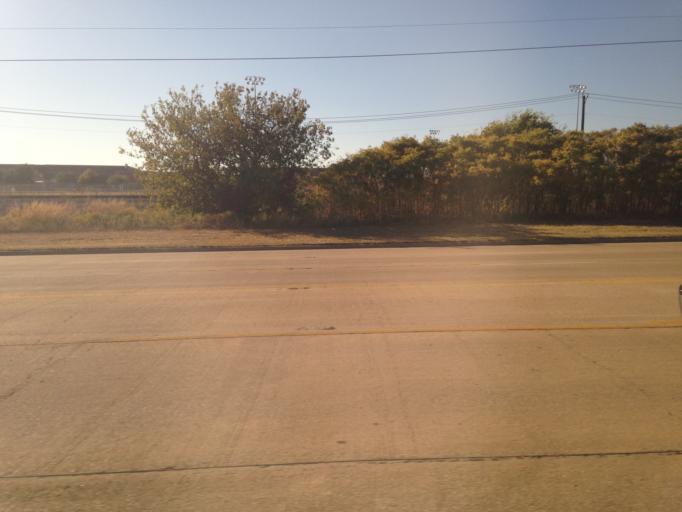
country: US
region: Texas
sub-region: Tarrant County
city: Watauga
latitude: 32.8894
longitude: -97.2594
